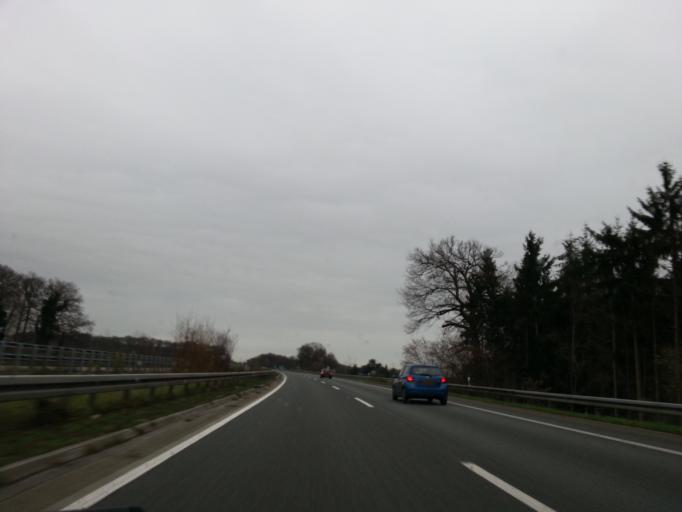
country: DE
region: North Rhine-Westphalia
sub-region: Regierungsbezirk Dusseldorf
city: Mehrhoog
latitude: 51.7811
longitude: 6.5079
